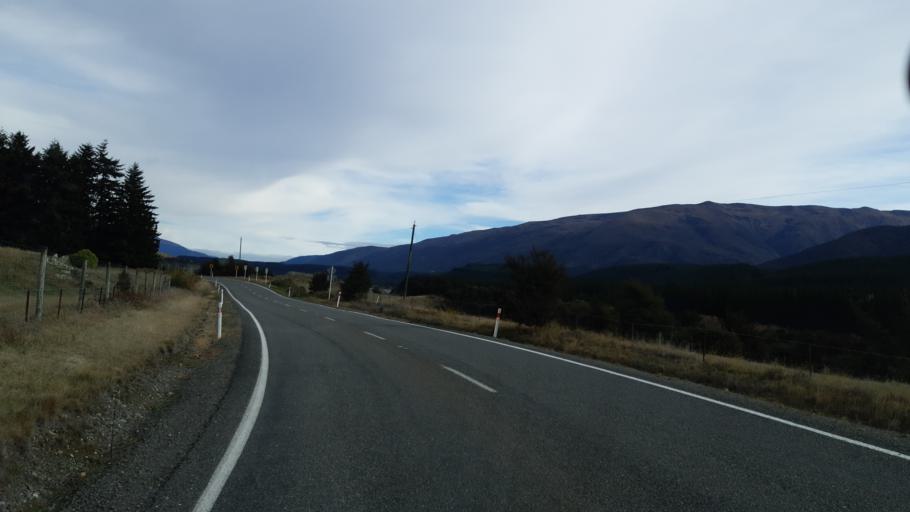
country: NZ
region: Tasman
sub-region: Tasman District
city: Brightwater
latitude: -41.6852
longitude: 173.1606
